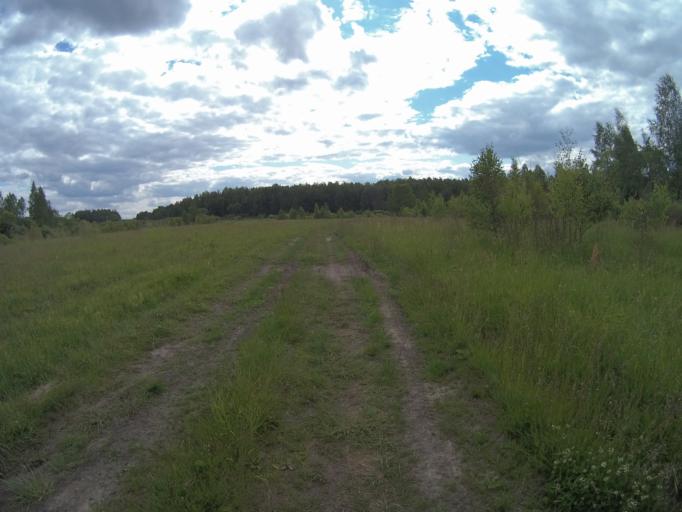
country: RU
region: Vladimir
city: Sudogda
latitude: 55.9596
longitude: 40.8217
